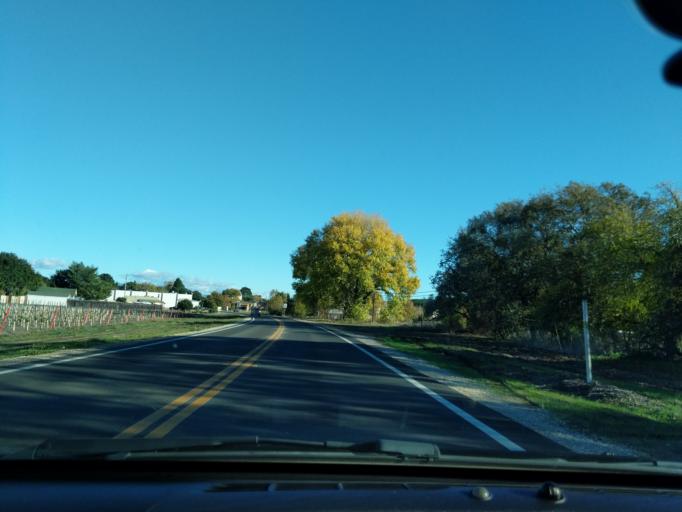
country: US
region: California
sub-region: Santa Barbara County
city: Los Alamos
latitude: 34.7447
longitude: -120.2854
